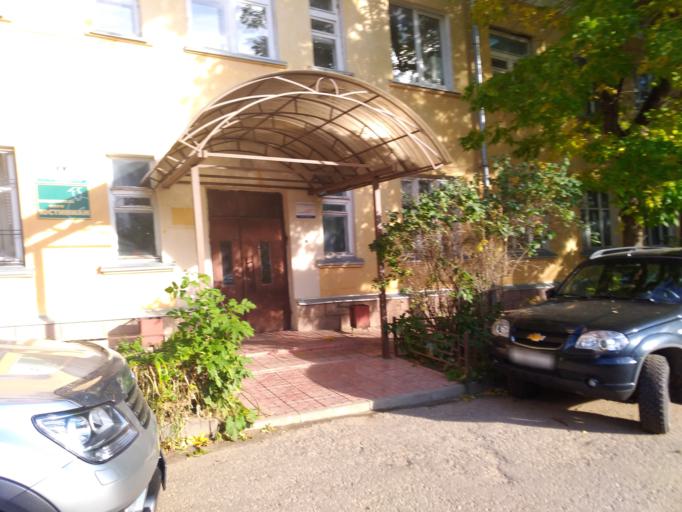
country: RU
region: Kaluga
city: Kaluga
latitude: 54.5115
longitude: 36.2530
